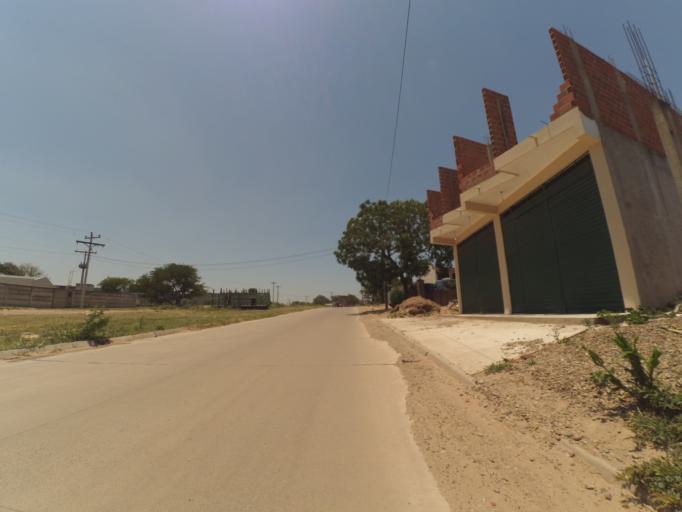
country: BO
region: Santa Cruz
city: Santa Cruz de la Sierra
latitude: -17.8470
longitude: -63.2432
